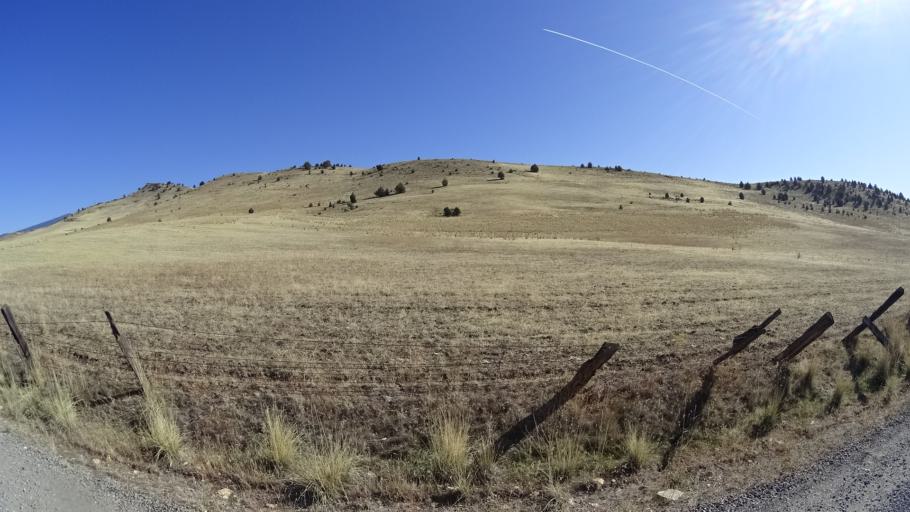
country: US
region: California
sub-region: Siskiyou County
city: Montague
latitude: 41.7383
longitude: -122.3683
